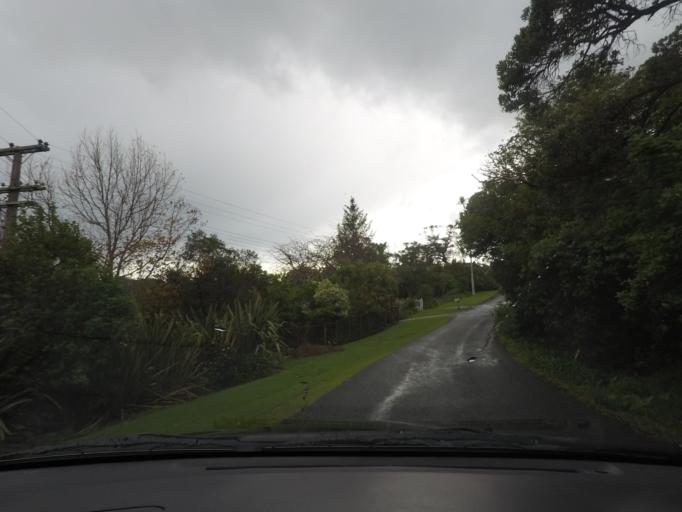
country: NZ
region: Auckland
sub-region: Auckland
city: Warkworth
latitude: -36.4743
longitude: 174.7360
